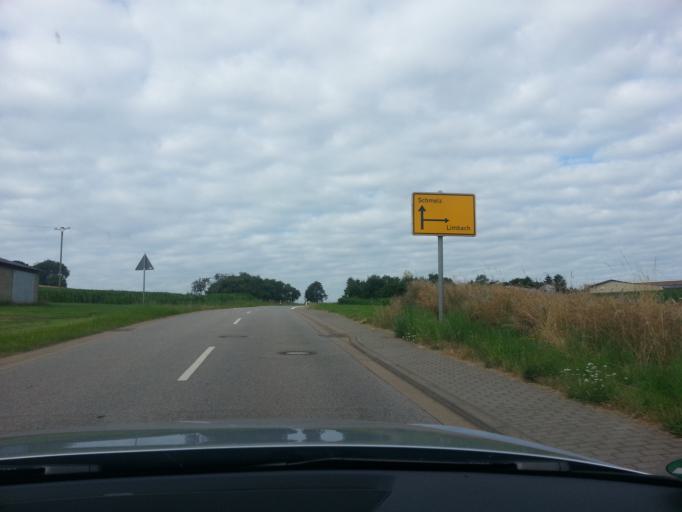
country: DE
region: Saarland
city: Lebach
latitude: 49.4503
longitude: 6.8919
